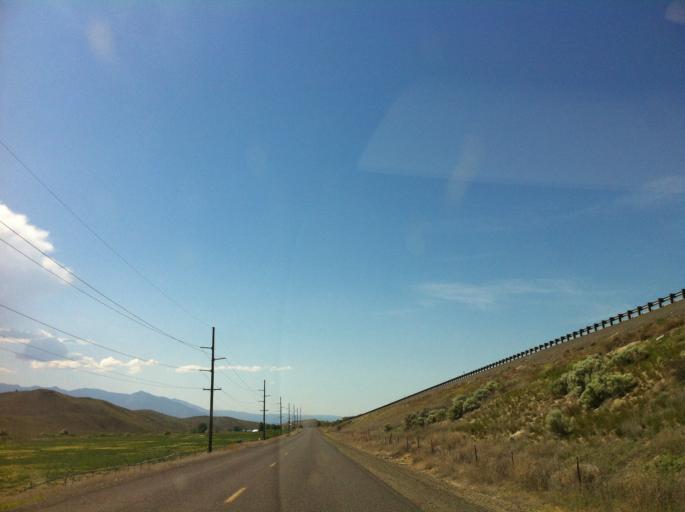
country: US
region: Oregon
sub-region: Baker County
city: Baker City
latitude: 44.7138
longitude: -117.7722
